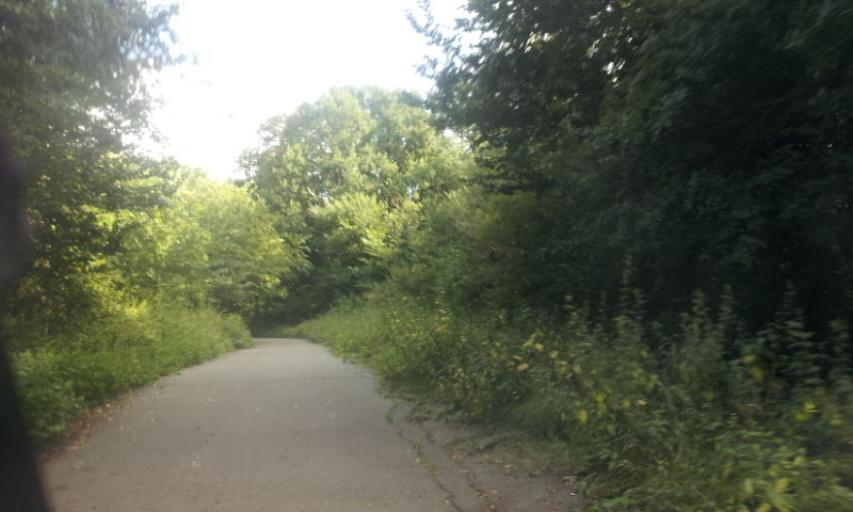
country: GB
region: England
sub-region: Greater London
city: Chislehurst
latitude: 51.3947
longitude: 0.0621
